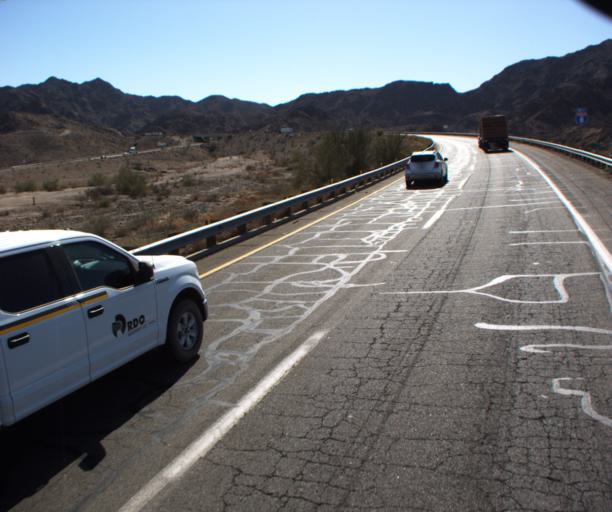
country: US
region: Arizona
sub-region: Yuma County
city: Fortuna Foothills
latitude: 32.6734
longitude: -114.3104
